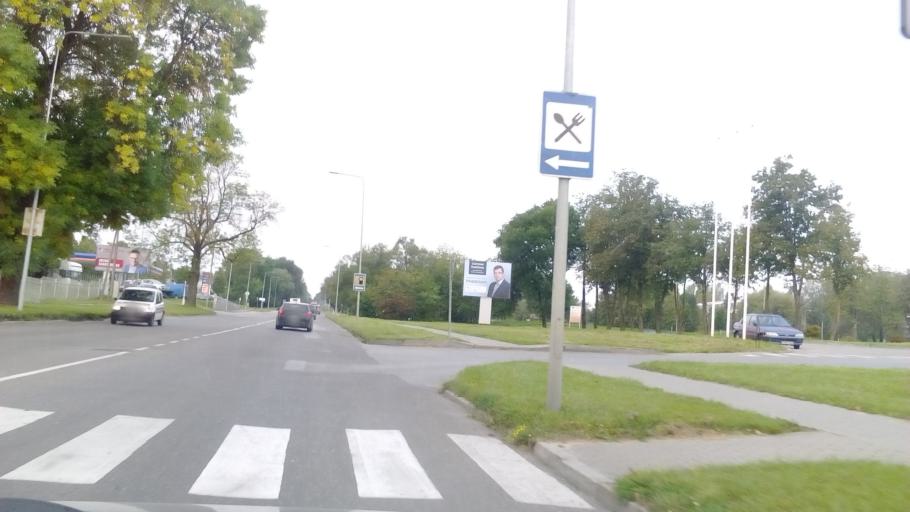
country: LT
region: Alytaus apskritis
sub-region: Alytus
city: Alytus
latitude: 54.3869
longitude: 24.0356
